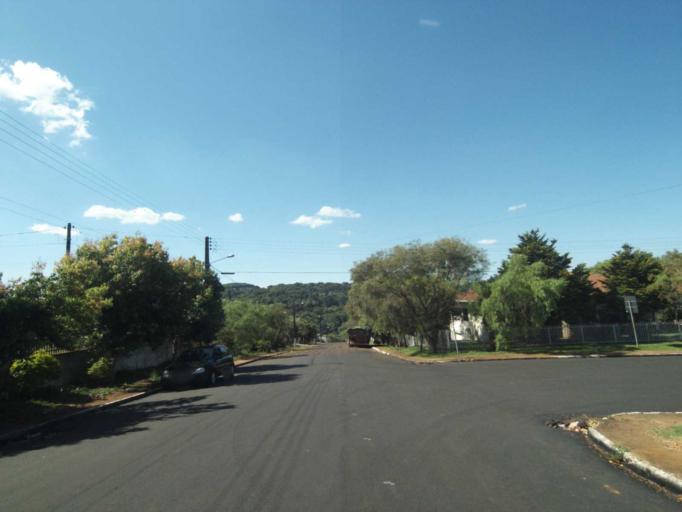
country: BR
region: Parana
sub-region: Laranjeiras Do Sul
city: Laranjeiras do Sul
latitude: -25.3820
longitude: -52.2058
